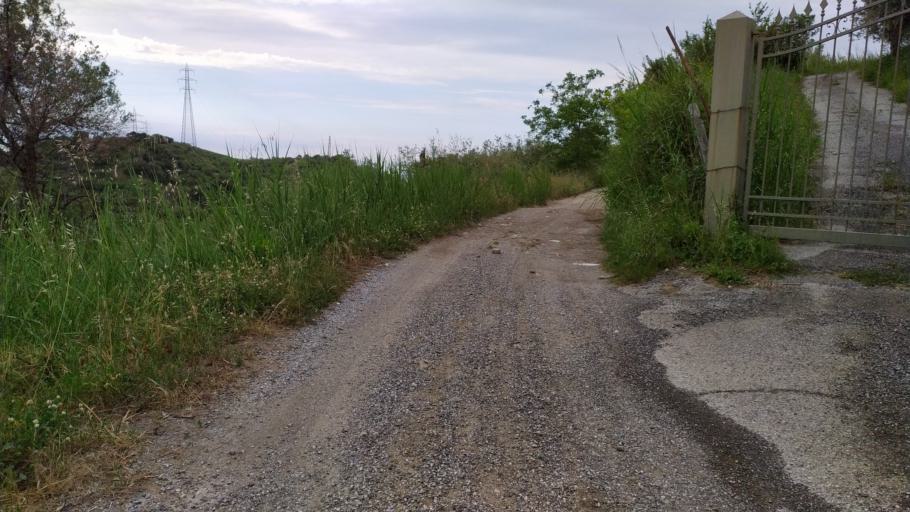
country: IT
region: Sicily
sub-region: Messina
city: Gualtieri Sicamino
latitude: 38.1556
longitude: 15.3007
